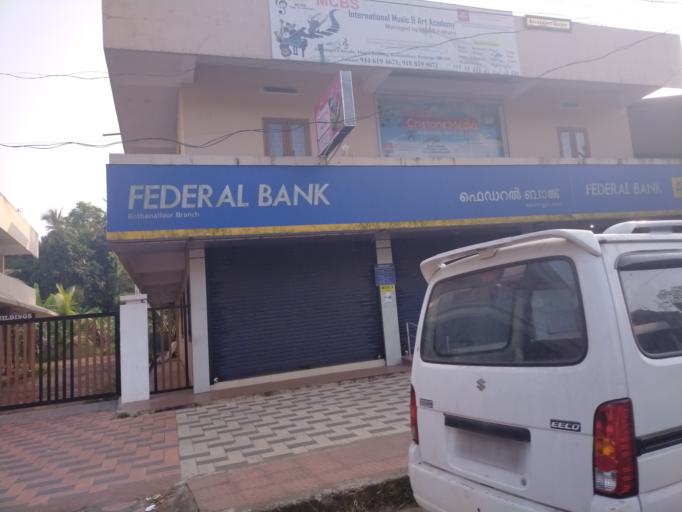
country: IN
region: Kerala
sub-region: Kottayam
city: Palackattumala
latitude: 9.7191
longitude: 76.5251
